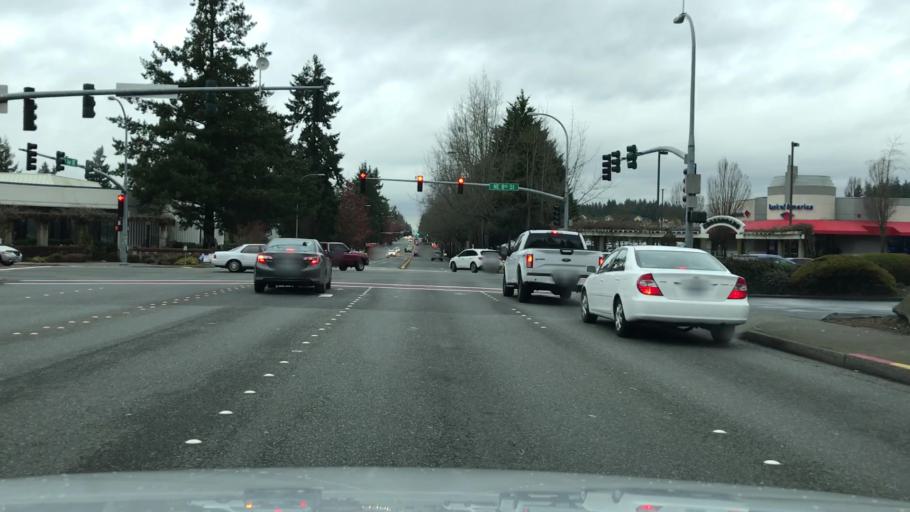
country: US
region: Washington
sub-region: King County
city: Eastgate
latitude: 47.6166
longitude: -122.1324
